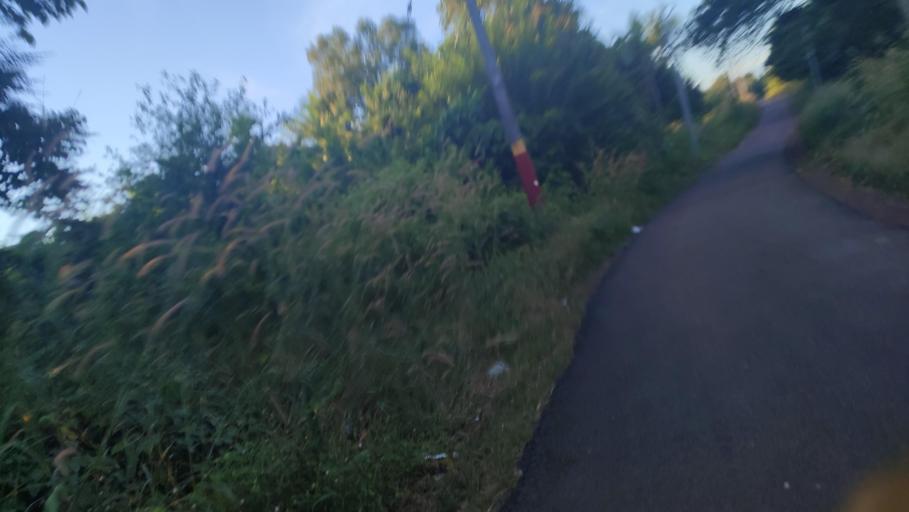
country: IN
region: Kerala
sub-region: Kasaragod District
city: Kannangad
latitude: 12.3988
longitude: 75.0607
